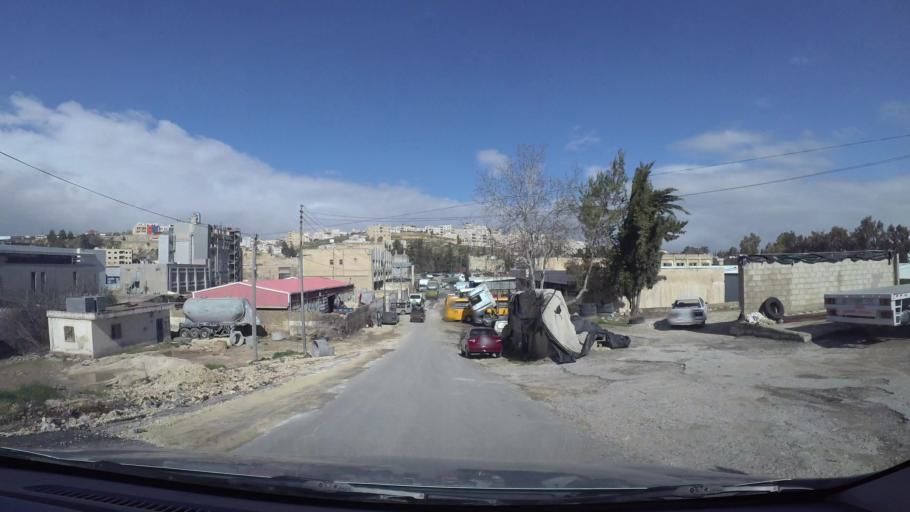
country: JO
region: Amman
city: Al Jubayhah
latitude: 32.0127
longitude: 35.8441
